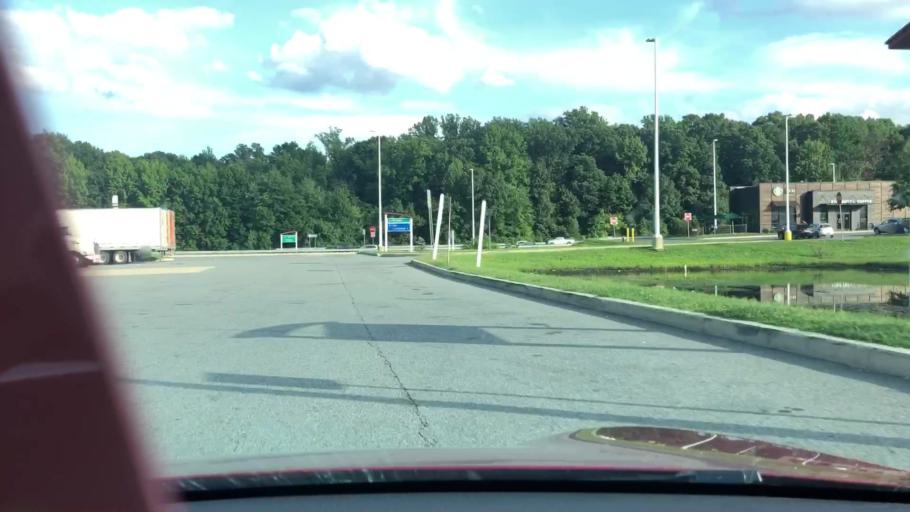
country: US
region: Delaware
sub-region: New Castle County
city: Brookside
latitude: 39.6639
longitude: -75.6898
